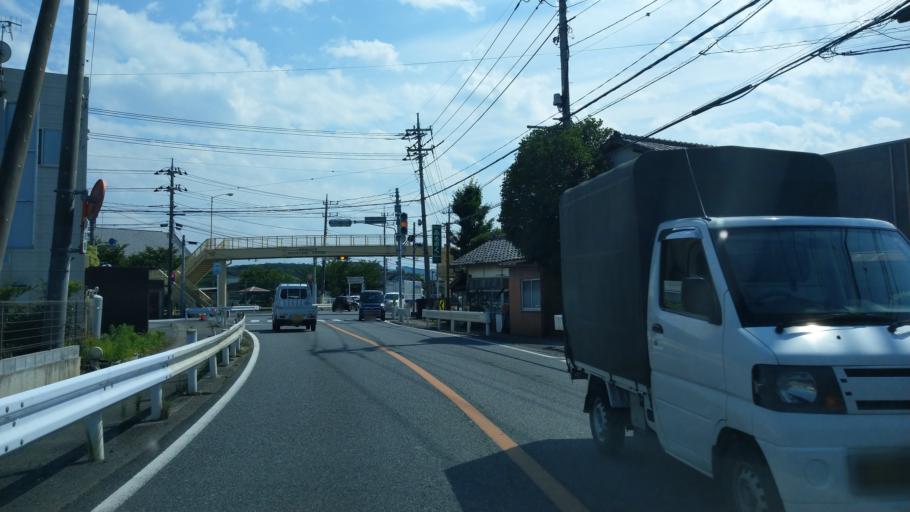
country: JP
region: Saitama
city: Kodamacho-kodamaminami
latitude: 36.2103
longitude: 139.1511
